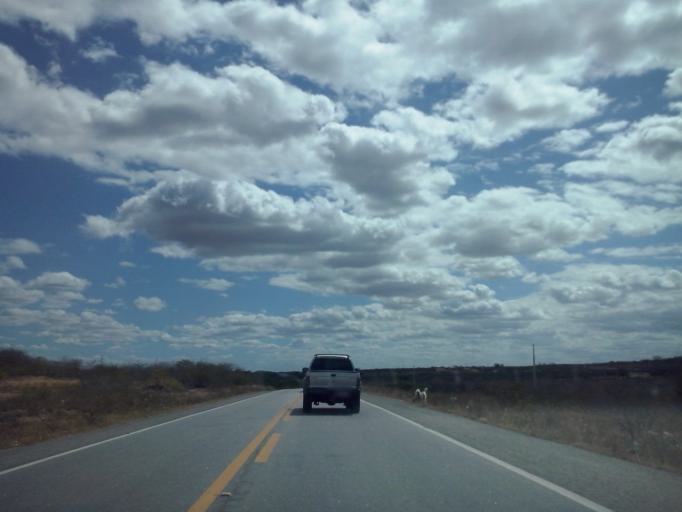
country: BR
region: Paraiba
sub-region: Soledade
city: Soledade
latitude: -7.0397
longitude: -36.4123
